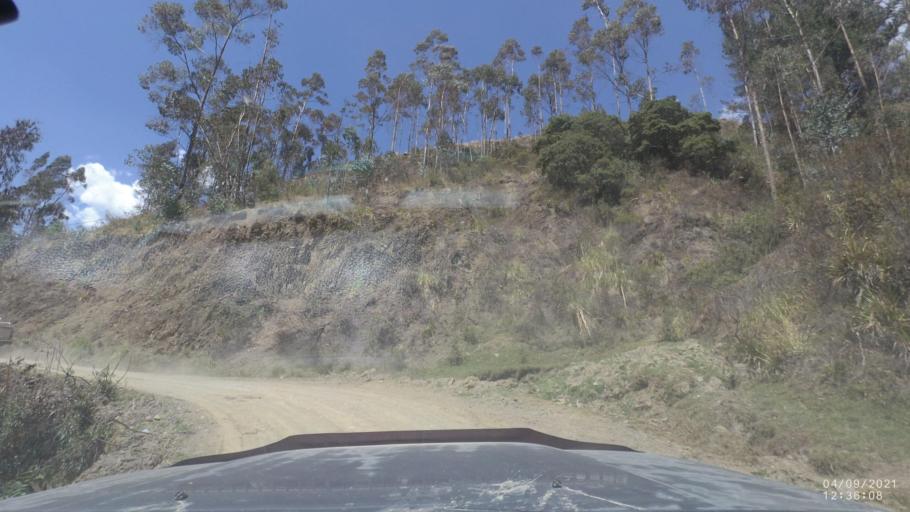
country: BO
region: Cochabamba
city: Colchani
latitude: -17.2242
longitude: -66.5083
